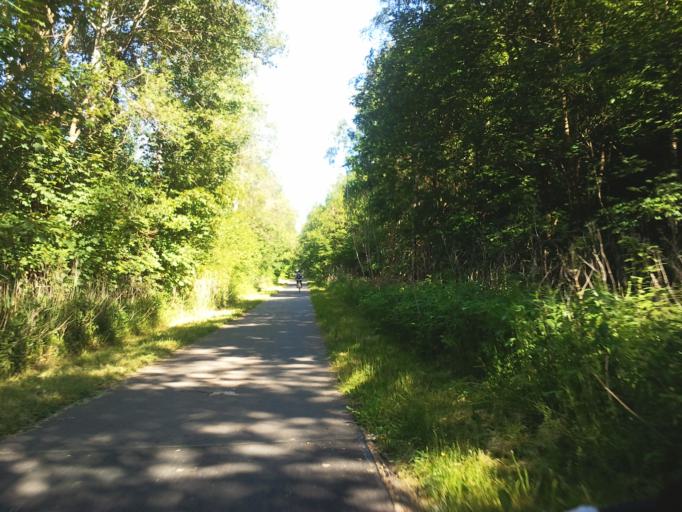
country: DE
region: Mecklenburg-Vorpommern
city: Nienhagen
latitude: 54.1907
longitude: 12.1834
